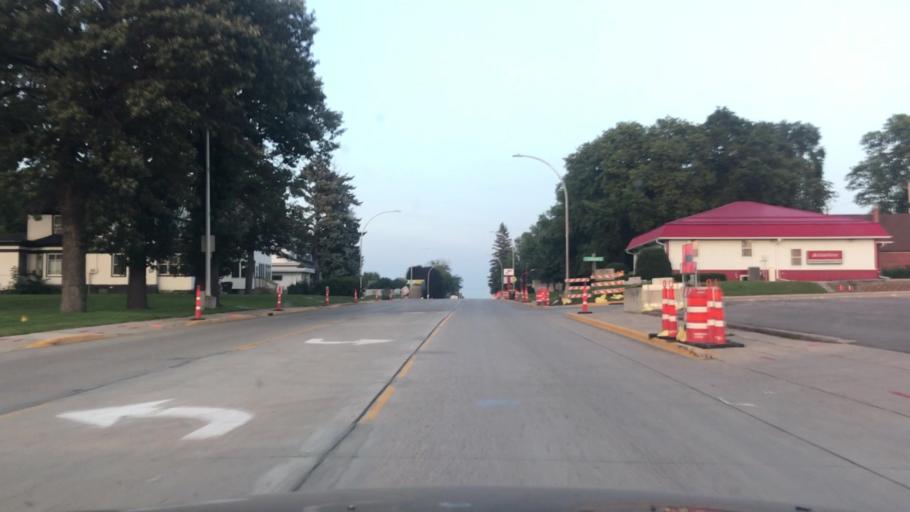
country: US
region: Minnesota
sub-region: Redwood County
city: Redwood Falls
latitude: 44.5413
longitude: -95.1168
